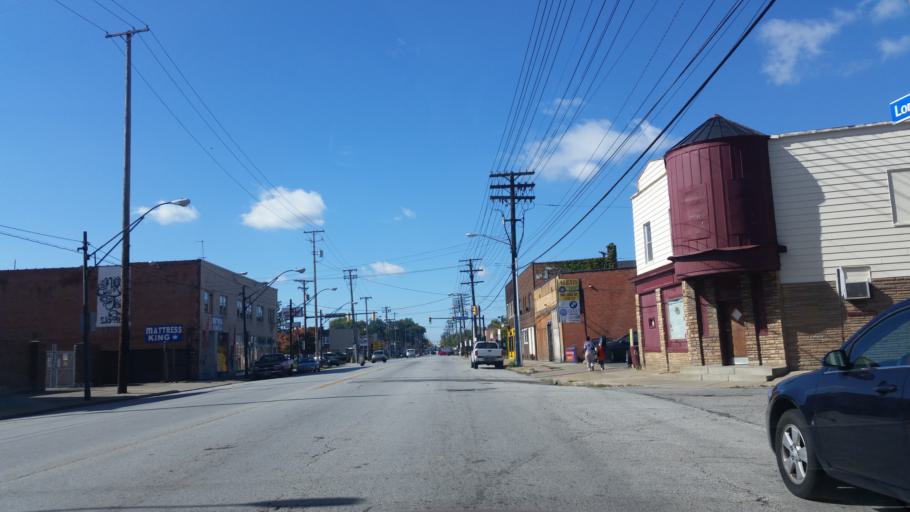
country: US
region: Ohio
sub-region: Cuyahoga County
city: Brooklyn
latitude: 41.4657
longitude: -81.7575
